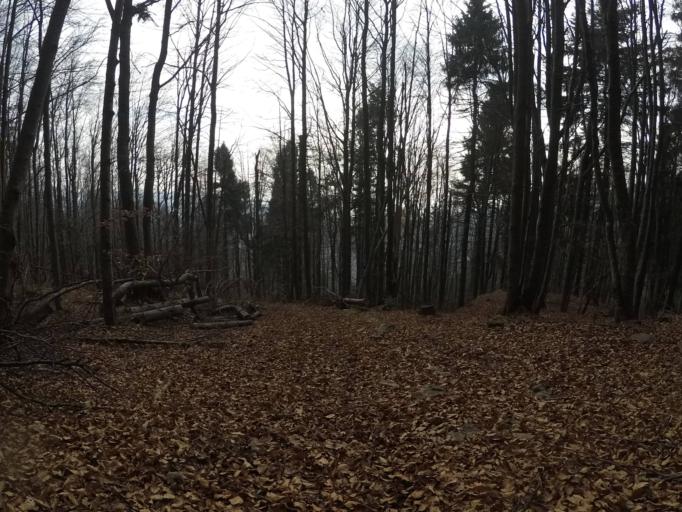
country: SK
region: Kosicky
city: Gelnica
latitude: 48.7751
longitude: 20.9516
